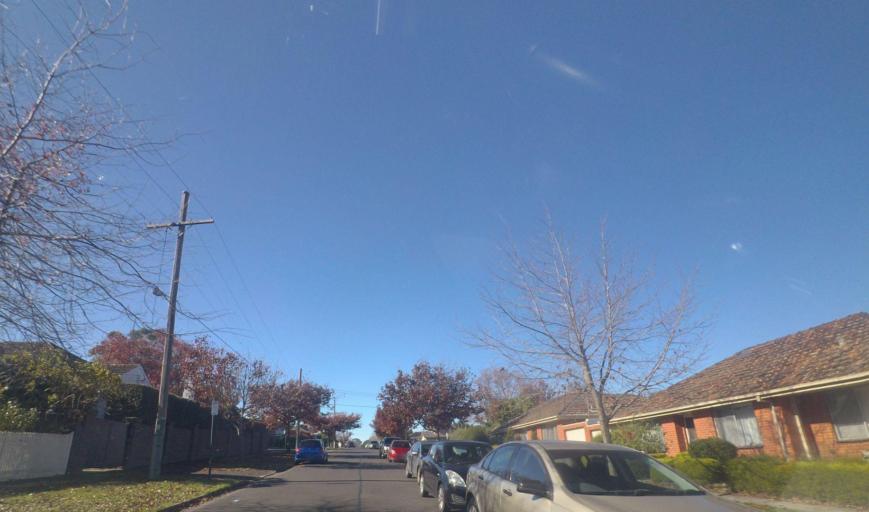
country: AU
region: Victoria
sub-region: Whitehorse
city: Box Hill
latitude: -37.8127
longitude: 145.1256
